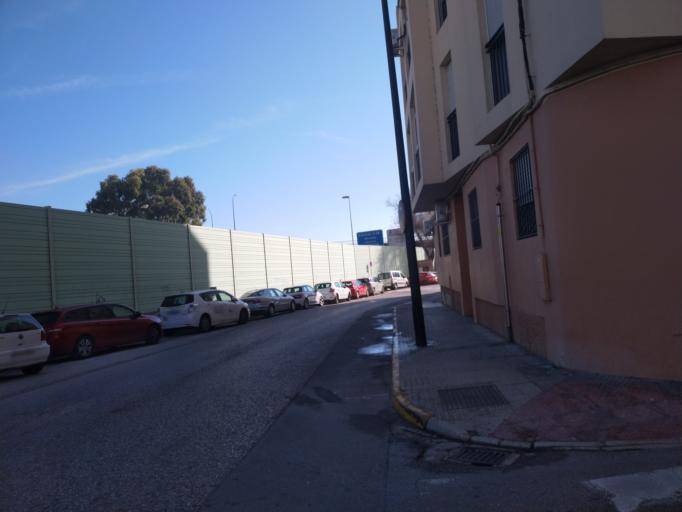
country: ES
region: Andalusia
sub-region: Provincia de Cadiz
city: San Fernando
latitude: 36.4724
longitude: -6.1901
